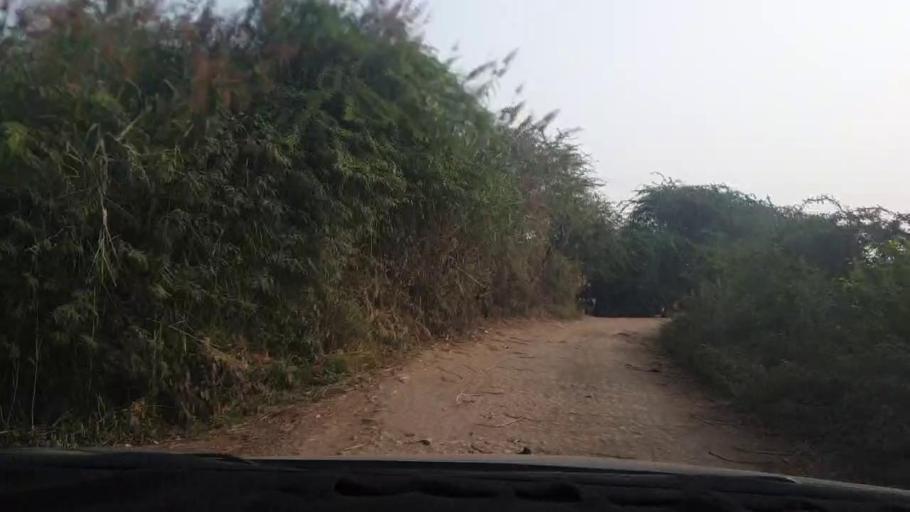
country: PK
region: Sindh
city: Matiari
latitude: 25.5939
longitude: 68.5394
